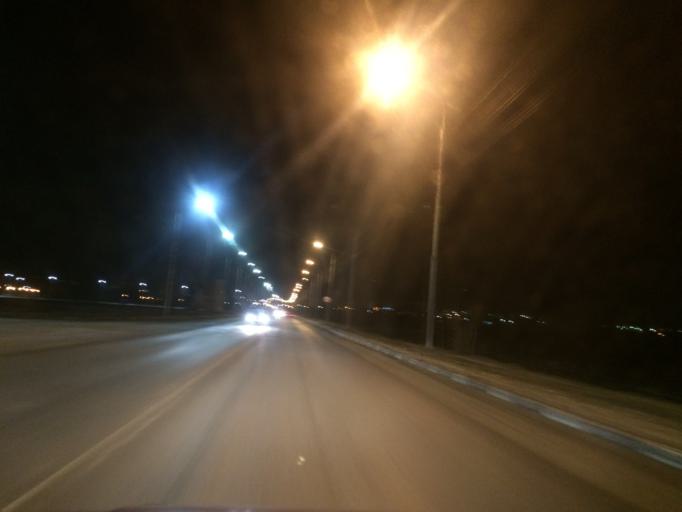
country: RU
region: Tula
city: Tula
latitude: 54.1854
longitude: 37.6522
